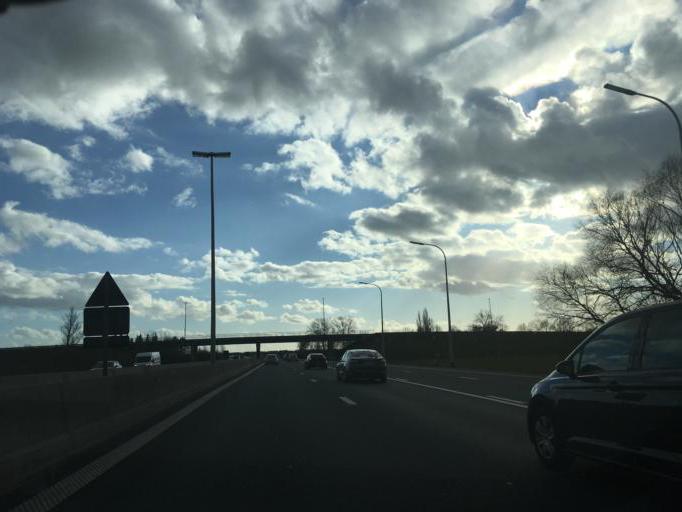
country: BE
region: Flanders
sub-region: Provincie West-Vlaanderen
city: Oostkamp
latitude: 51.1485
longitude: 3.2063
